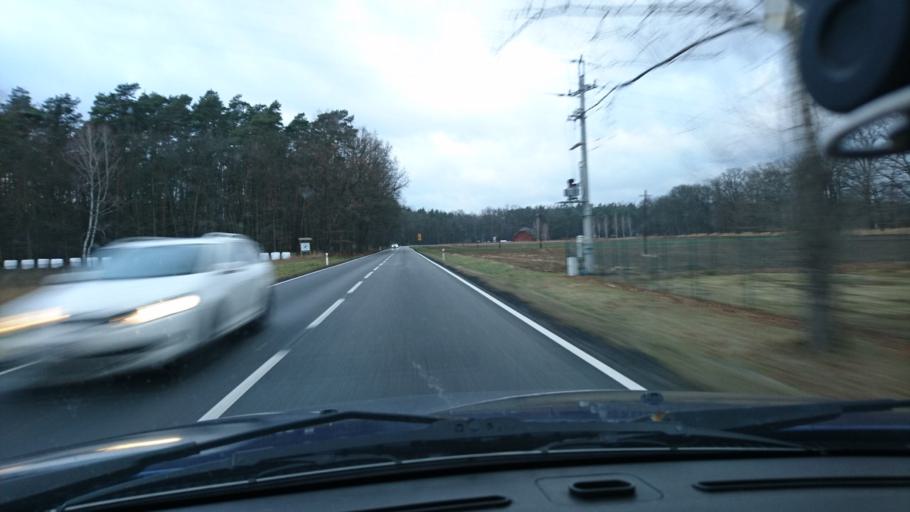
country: PL
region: Opole Voivodeship
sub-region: Powiat oleski
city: Olesno
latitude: 50.9189
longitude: 18.3427
